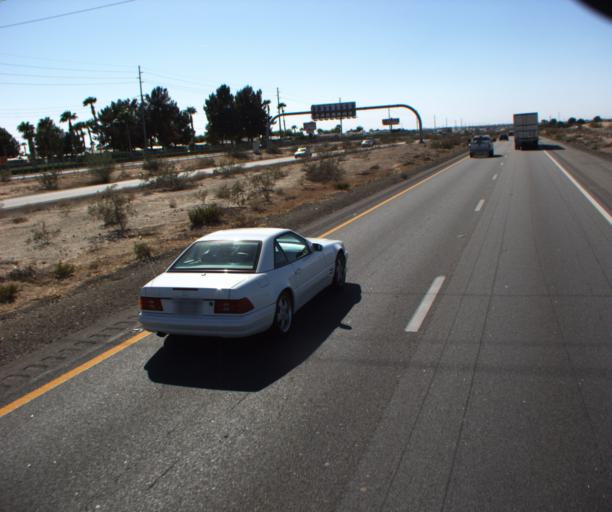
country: US
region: Arizona
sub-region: Yuma County
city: Fortuna Foothills
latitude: 32.6708
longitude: -114.4609
